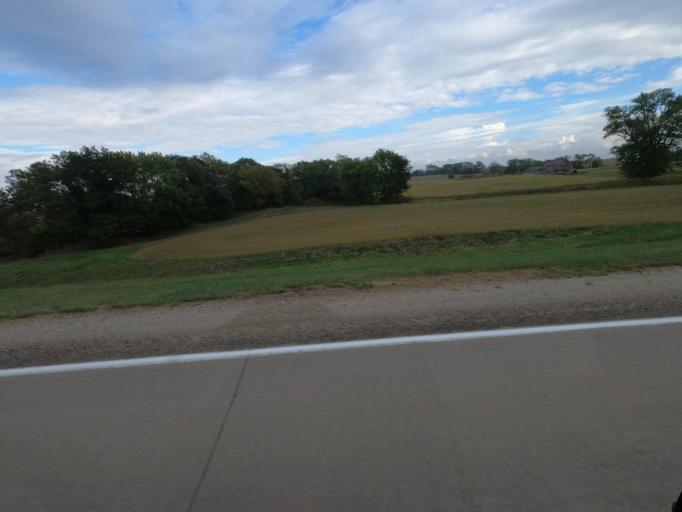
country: US
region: Iowa
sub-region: Henry County
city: Mount Pleasant
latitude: 40.8086
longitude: -91.7037
